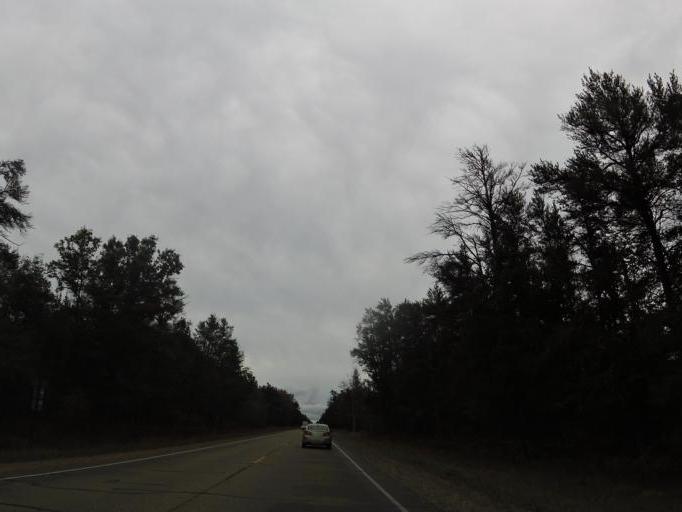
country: US
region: Michigan
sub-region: Roscommon County
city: Roscommon
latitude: 44.4847
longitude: -84.5691
